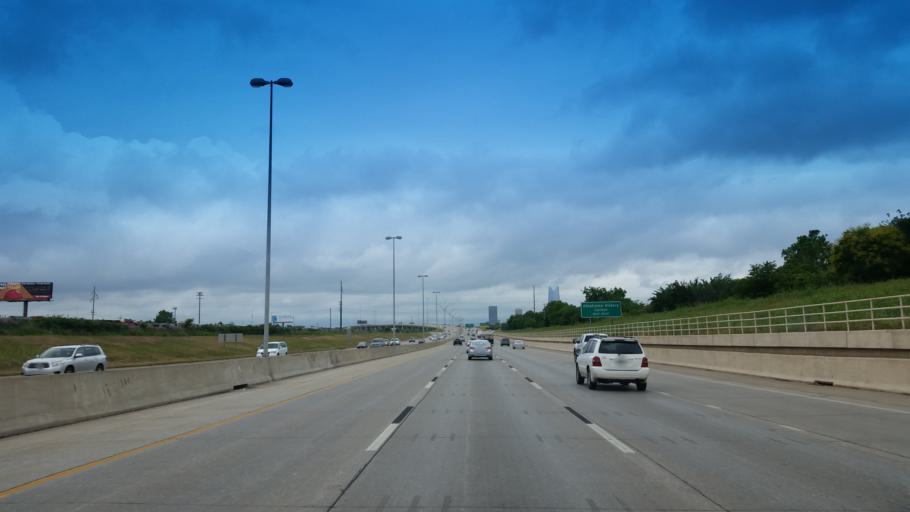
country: US
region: Oklahoma
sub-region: Oklahoma County
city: Oklahoma City
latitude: 35.5037
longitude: -97.5142
